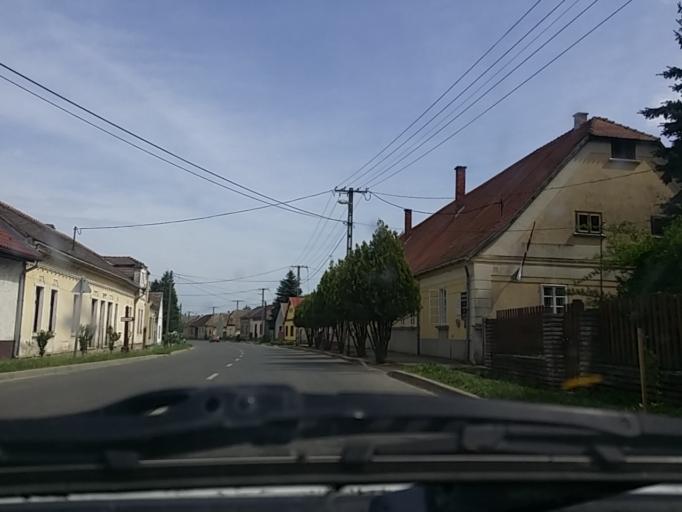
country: HU
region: Baranya
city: Vajszlo
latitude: 45.8589
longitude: 17.9848
